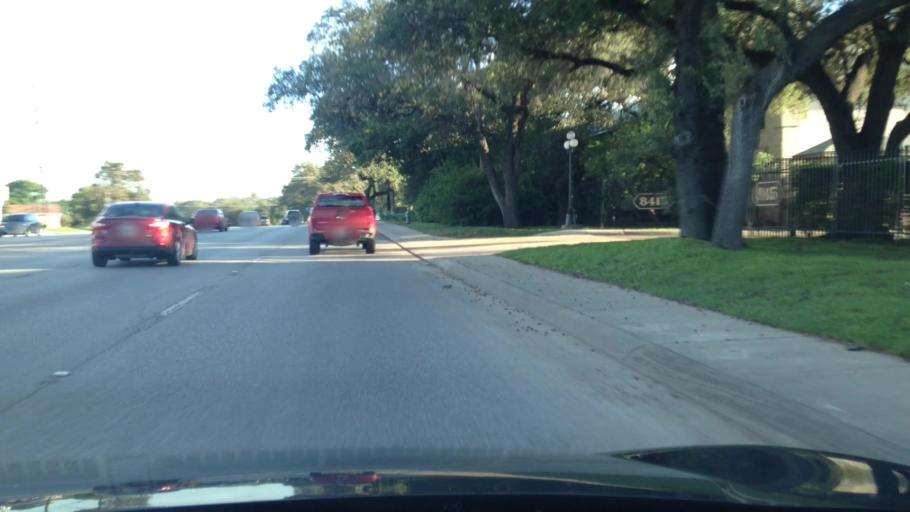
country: US
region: Texas
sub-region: Bexar County
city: Balcones Heights
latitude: 29.5182
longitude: -98.5728
